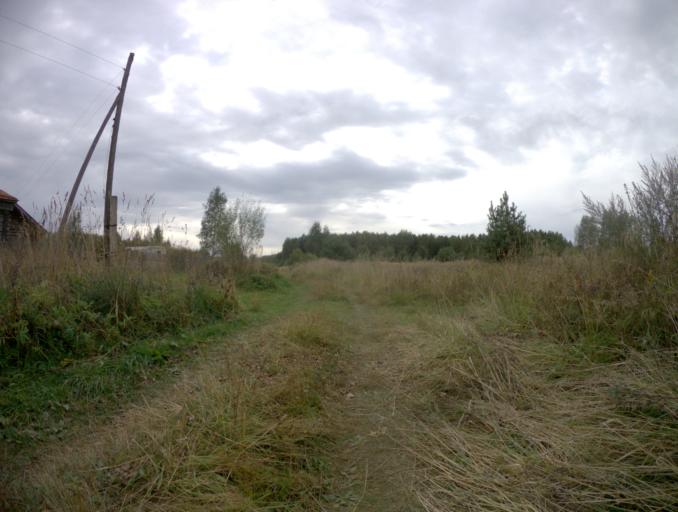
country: RU
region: Vladimir
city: Urshel'skiy
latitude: 55.8533
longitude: 40.2095
